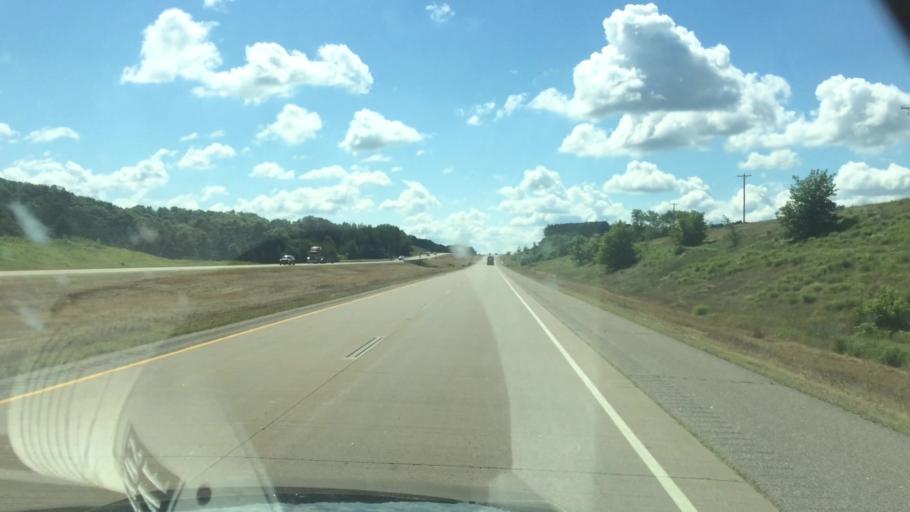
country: US
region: Wisconsin
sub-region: Portage County
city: Amherst
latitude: 44.4212
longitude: -89.2550
